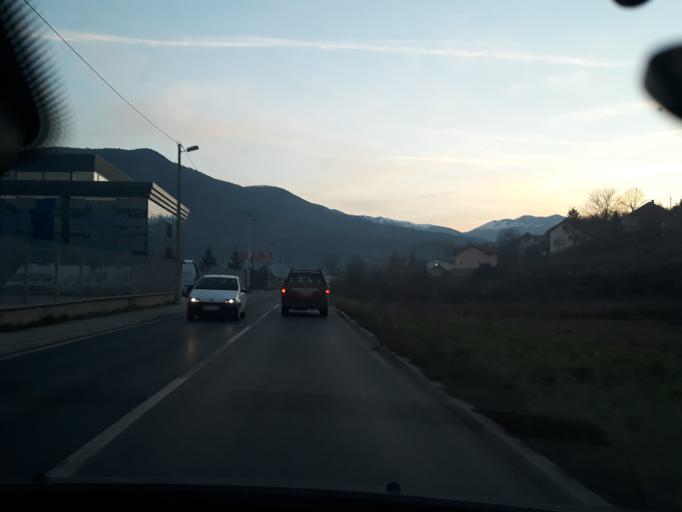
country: BA
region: Federation of Bosnia and Herzegovina
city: Hadzici
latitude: 43.8562
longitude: 18.2499
